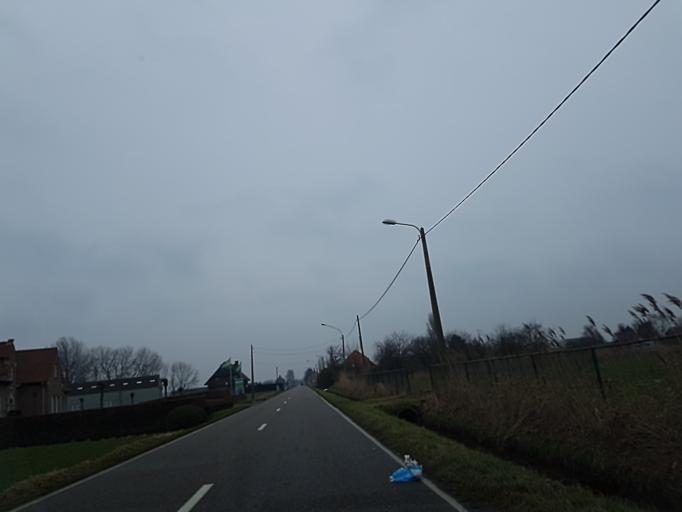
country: BE
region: Flanders
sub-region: Provincie Antwerpen
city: Stabroek
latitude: 51.3150
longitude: 4.3833
